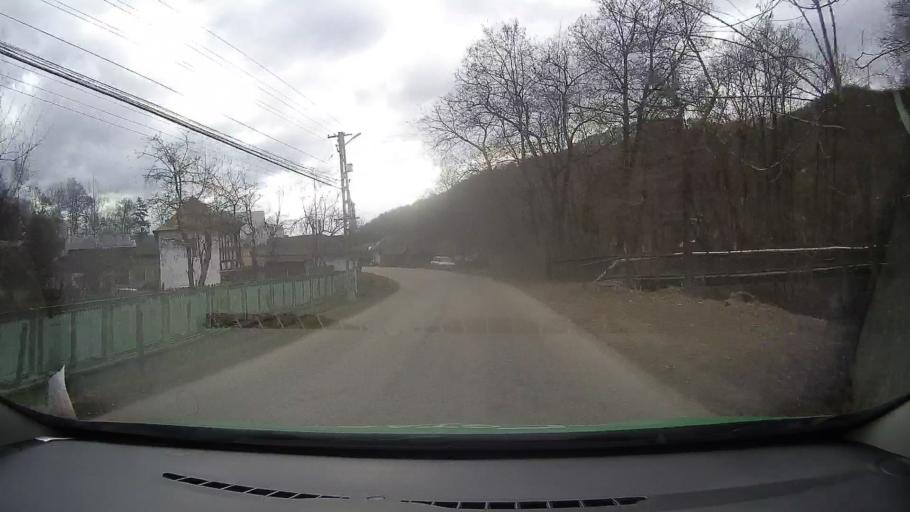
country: RO
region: Dambovita
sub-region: Comuna Visinesti
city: Visinesti
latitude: 45.1017
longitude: 25.5642
